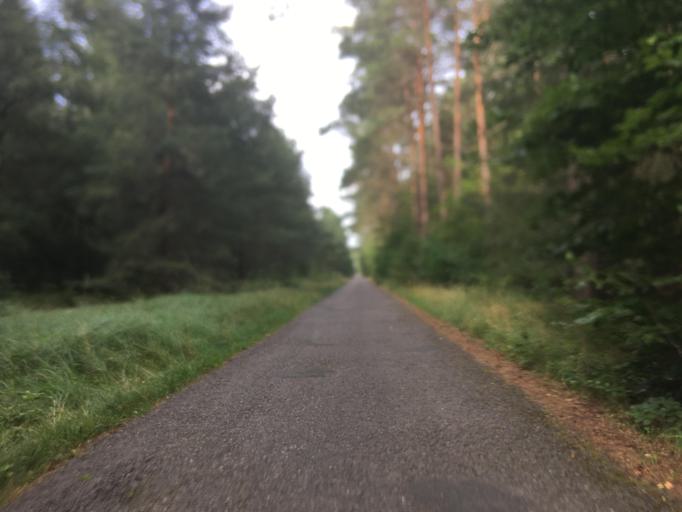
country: DE
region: Brandenburg
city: Melchow
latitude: 52.8021
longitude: 13.6957
